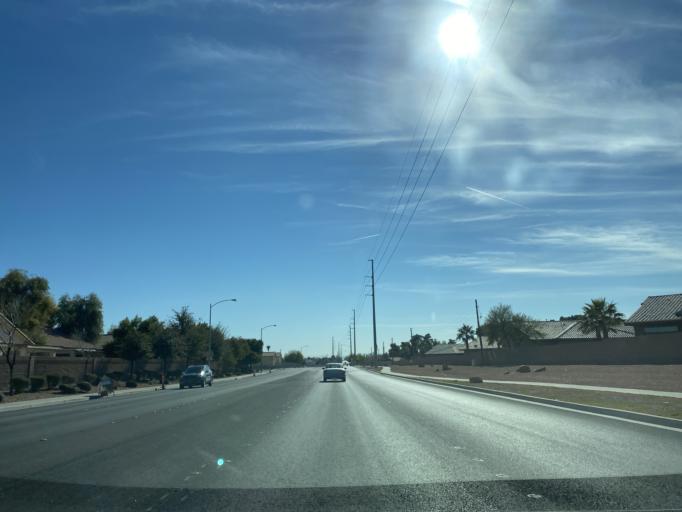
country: US
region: Nevada
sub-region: Clark County
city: North Las Vegas
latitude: 36.2462
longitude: -115.1438
